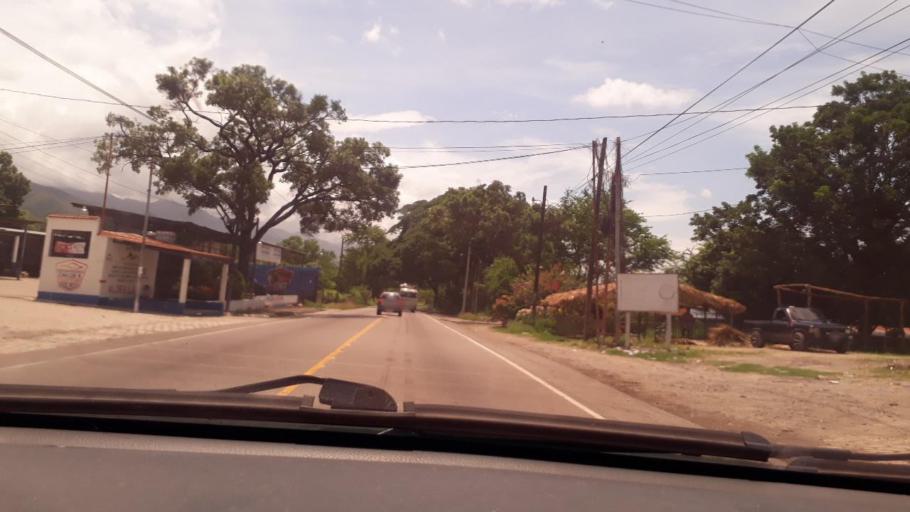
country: GT
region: Zacapa
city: Rio Hondo
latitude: 15.0499
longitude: -89.5661
